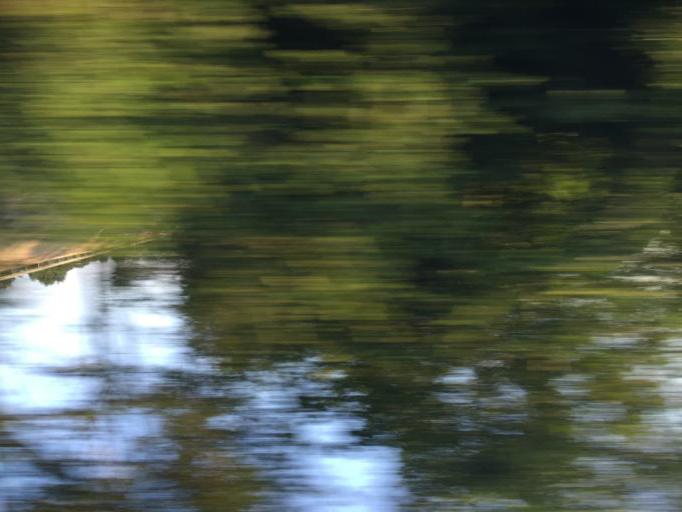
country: DE
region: North Rhine-Westphalia
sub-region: Regierungsbezirk Munster
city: Muenster
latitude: 52.0153
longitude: 7.5861
